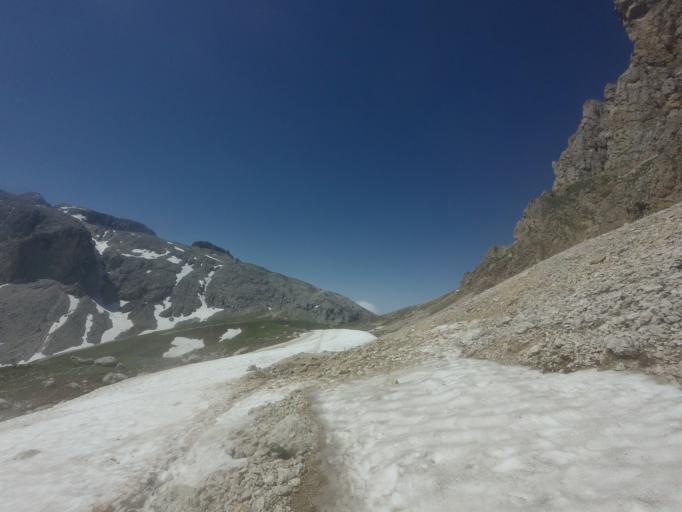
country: IT
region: Trentino-Alto Adige
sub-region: Provincia di Trento
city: Mazzin
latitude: 46.4990
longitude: 11.6360
